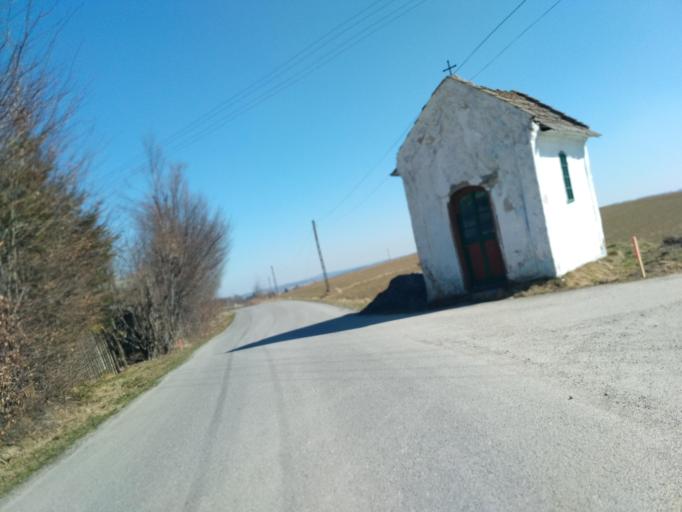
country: PL
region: Subcarpathian Voivodeship
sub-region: Powiat ropczycko-sedziszowski
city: Niedzwiada
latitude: 49.9512
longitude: 21.5255
